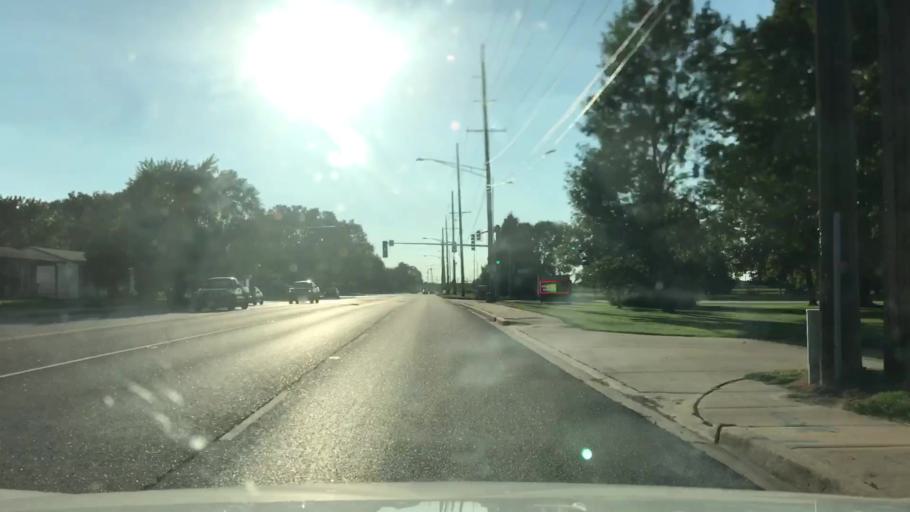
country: US
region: Illinois
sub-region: Madison County
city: Granite City
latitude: 38.7316
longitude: -90.1302
